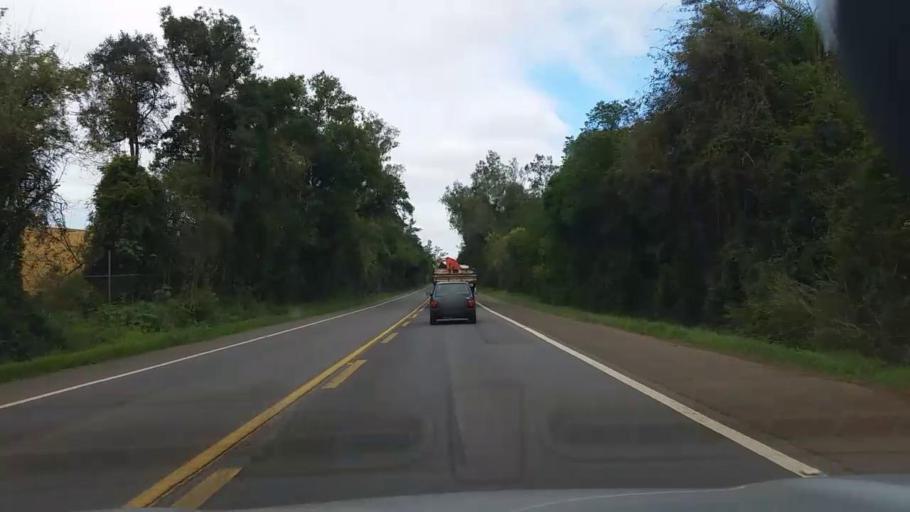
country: BR
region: Rio Grande do Sul
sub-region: Lajeado
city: Lajeado
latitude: -29.4175
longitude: -52.0243
